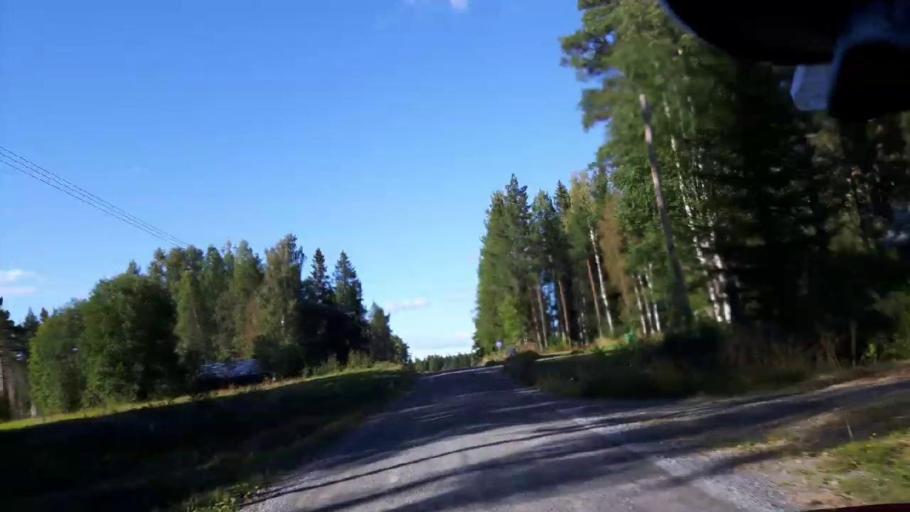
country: SE
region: Jaemtland
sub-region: Ragunda Kommun
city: Hammarstrand
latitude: 63.5205
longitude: 16.0563
